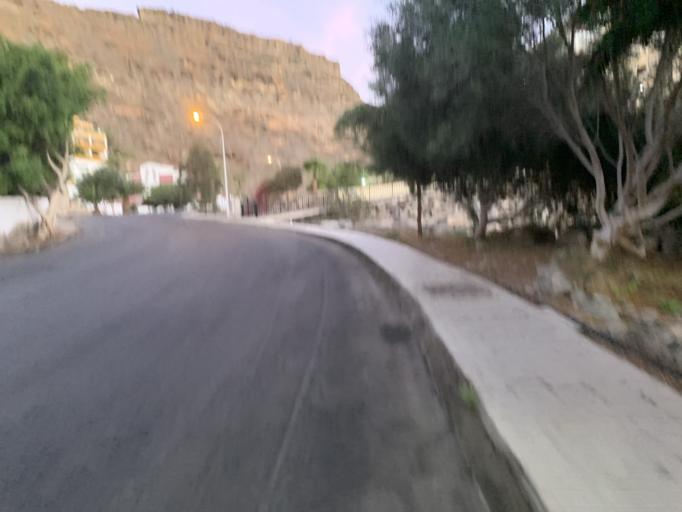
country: ES
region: Canary Islands
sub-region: Provincia de Las Palmas
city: Puerto Rico
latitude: 27.8027
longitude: -15.7318
